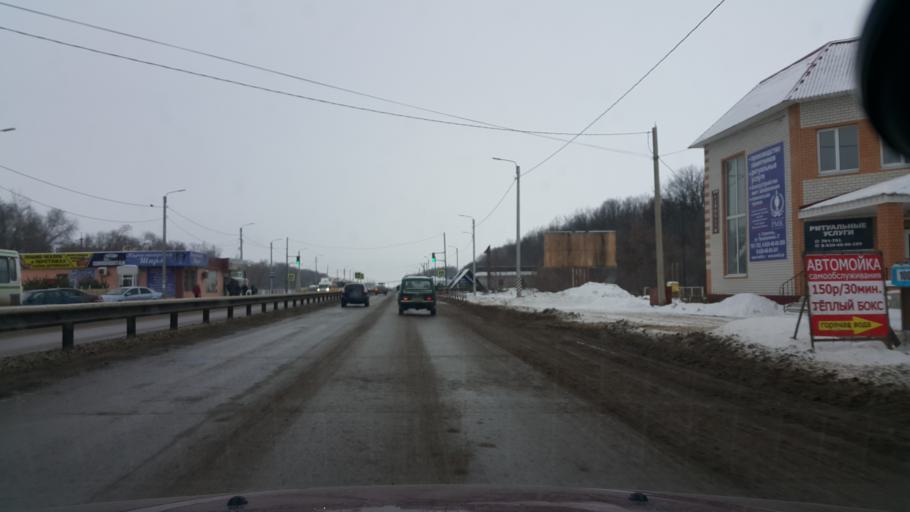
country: RU
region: Tambov
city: Bokino
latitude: 52.6447
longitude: 41.4419
